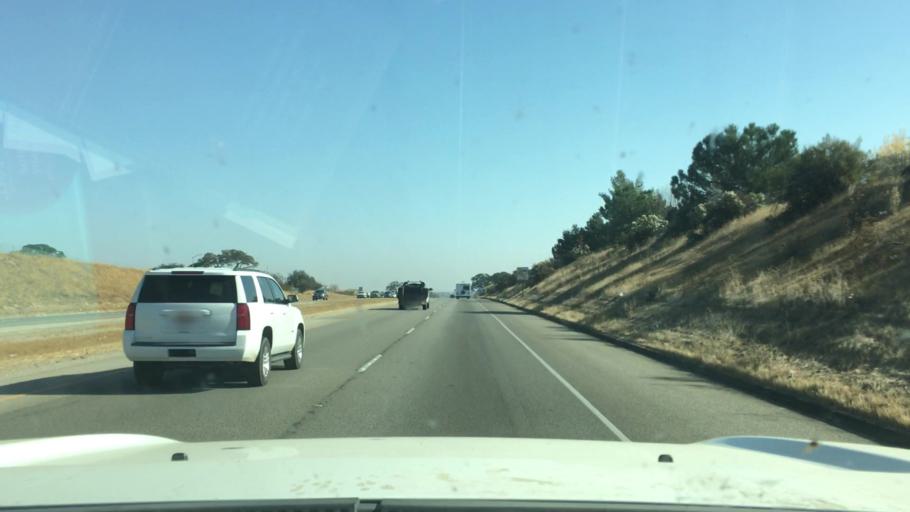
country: US
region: California
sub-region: San Luis Obispo County
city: Paso Robles
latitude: 35.6445
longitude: -120.6668
